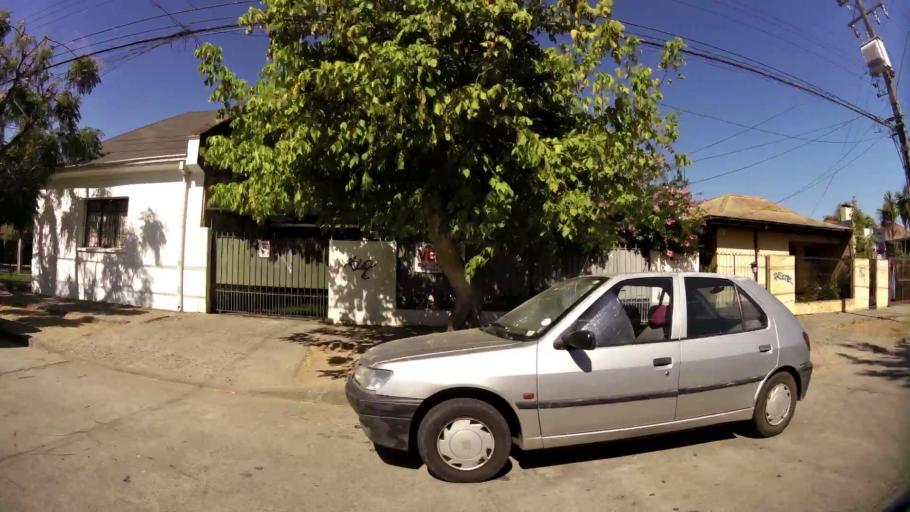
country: CL
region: Maule
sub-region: Provincia de Talca
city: Talca
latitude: -35.4331
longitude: -71.6646
